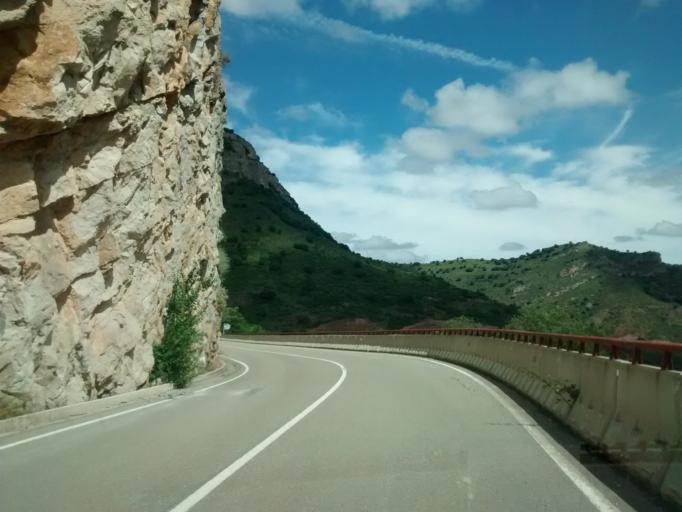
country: ES
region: La Rioja
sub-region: Provincia de La Rioja
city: Leza de Rio Leza
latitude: 42.3120
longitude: -2.4142
